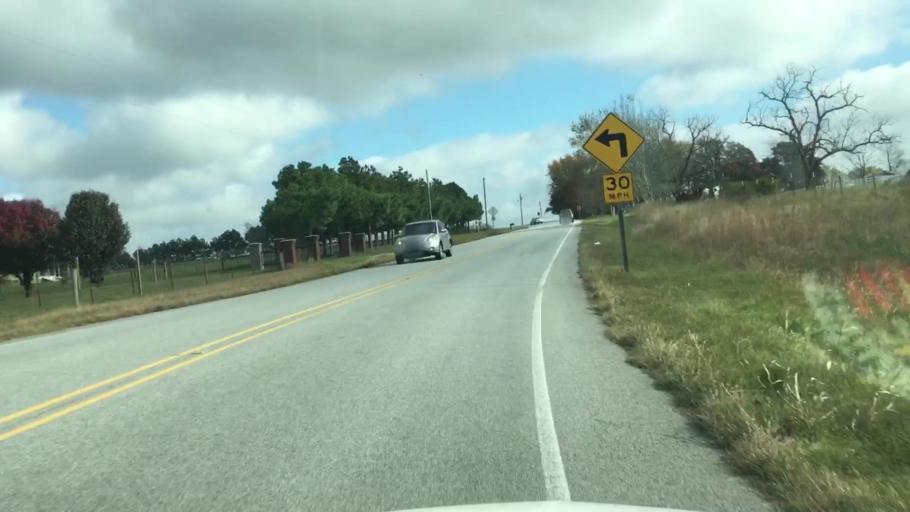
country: US
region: Arkansas
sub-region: Benton County
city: Centerton
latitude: 36.2869
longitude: -94.3487
